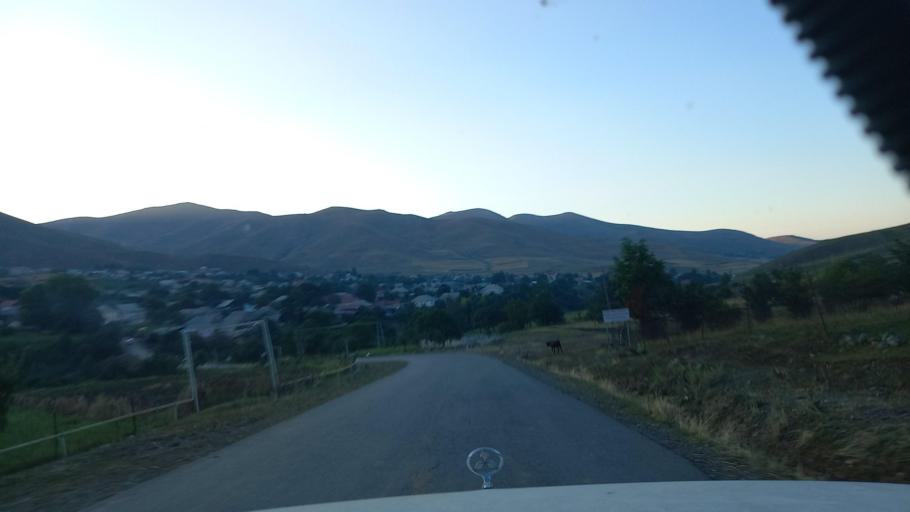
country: AZ
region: Tovuz
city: Cobansignaq
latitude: 40.6834
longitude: 45.7671
